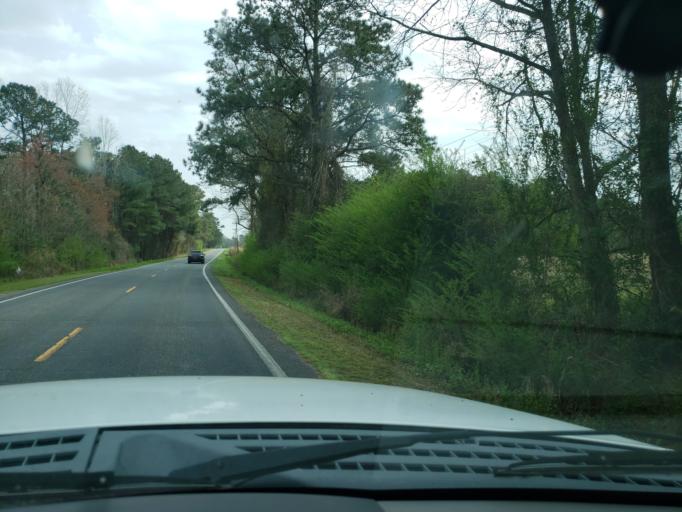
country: US
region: North Carolina
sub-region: Duplin County
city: Beulaville
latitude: 34.7698
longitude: -77.8057
